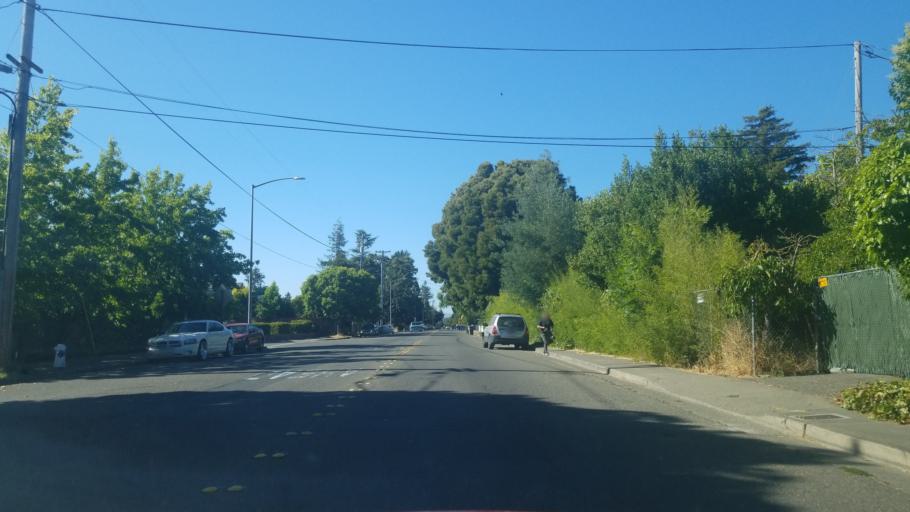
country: US
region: California
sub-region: Sonoma County
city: Roseland
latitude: 38.4194
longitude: -122.7240
